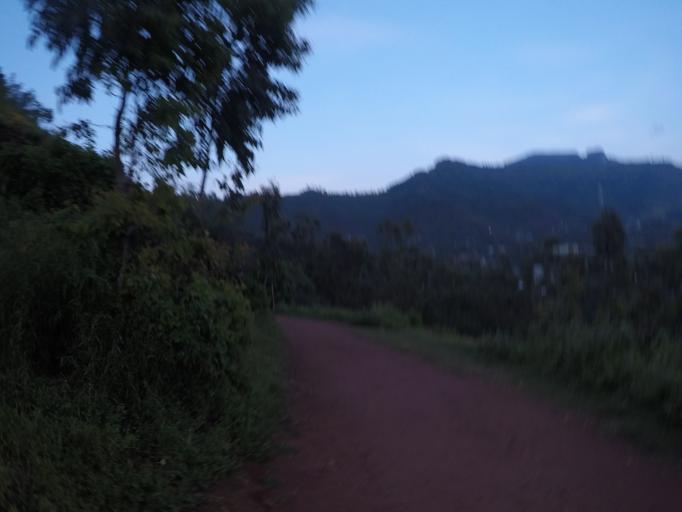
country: ET
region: Amhara
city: Lalibela
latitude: 12.0308
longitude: 39.0456
